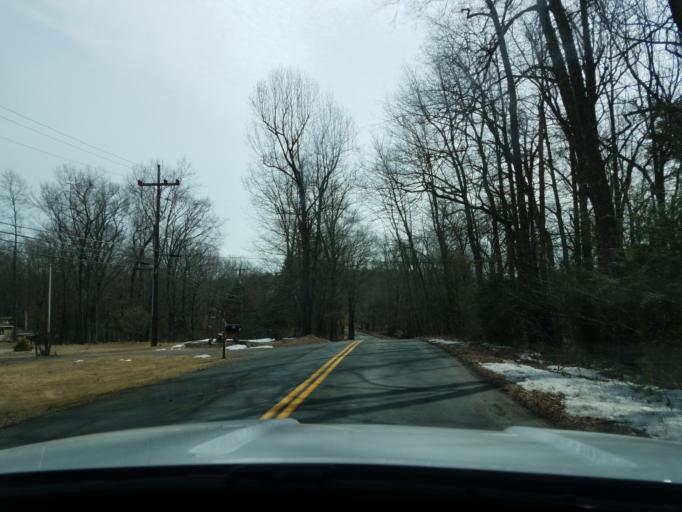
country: US
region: Connecticut
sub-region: Hartford County
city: Collinsville
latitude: 41.7773
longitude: -72.9081
